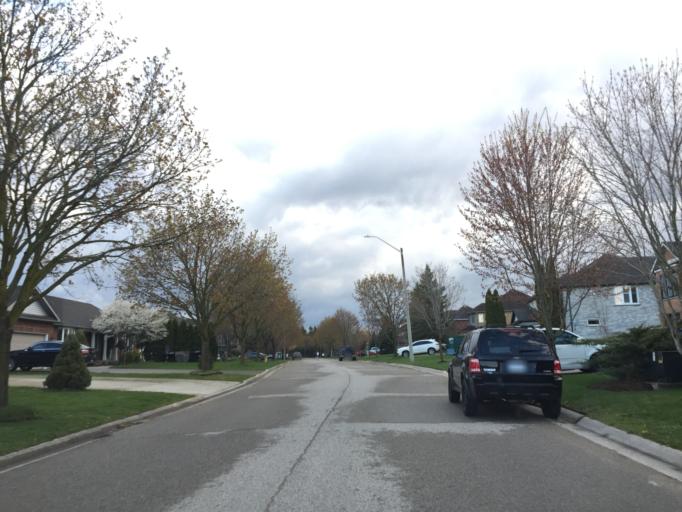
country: CA
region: Ontario
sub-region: Wellington County
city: Guelph
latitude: 43.5783
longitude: -80.2796
